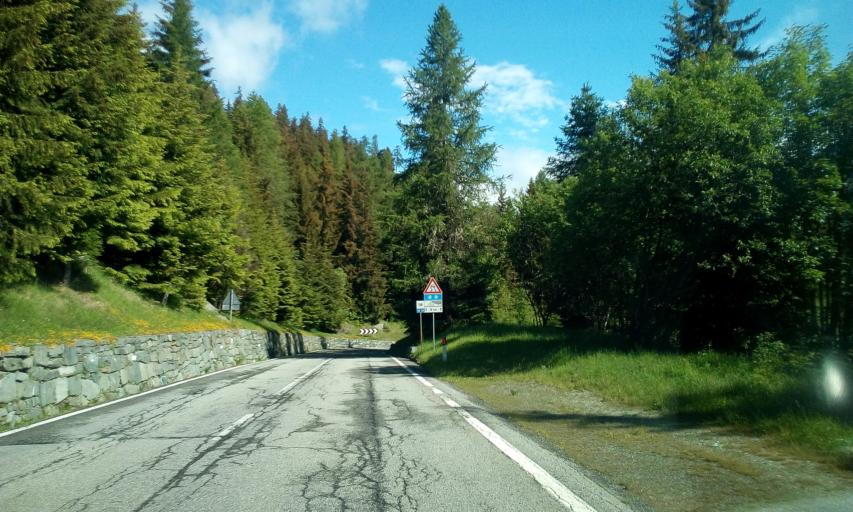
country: IT
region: Aosta Valley
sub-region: Valle d'Aosta
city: Brusson
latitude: 45.7583
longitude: 7.7087
